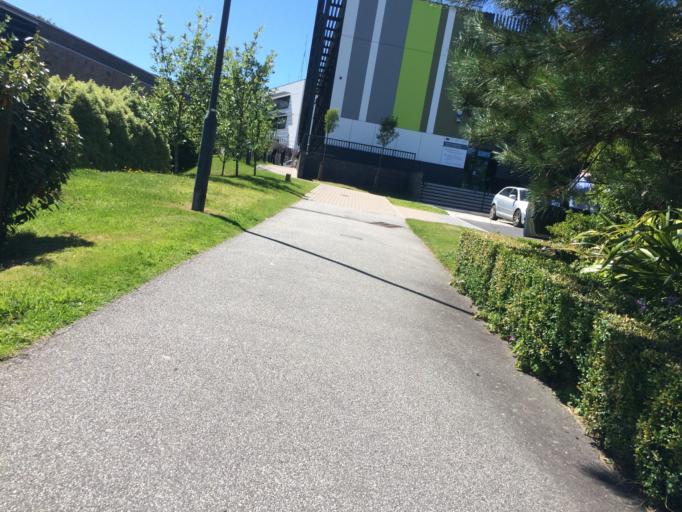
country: GB
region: England
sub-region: Cornwall
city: Penryn
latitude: 50.1713
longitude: -5.1258
